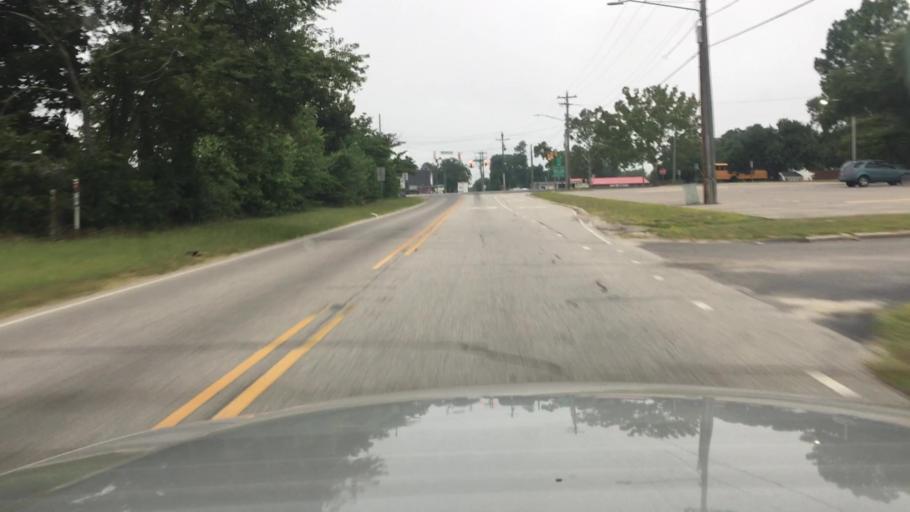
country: US
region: North Carolina
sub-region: Cumberland County
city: Fayetteville
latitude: 35.0129
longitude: -78.8956
